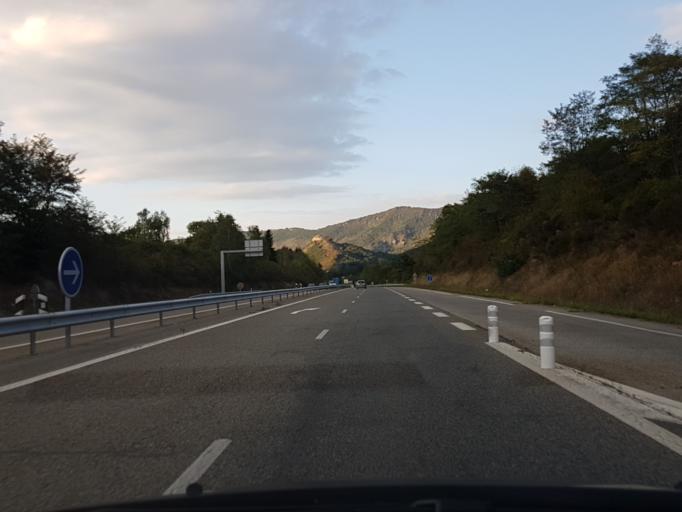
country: FR
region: Midi-Pyrenees
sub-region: Departement de l'Ariege
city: Saint-Paul-de-Jarrat
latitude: 42.9096
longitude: 1.6388
